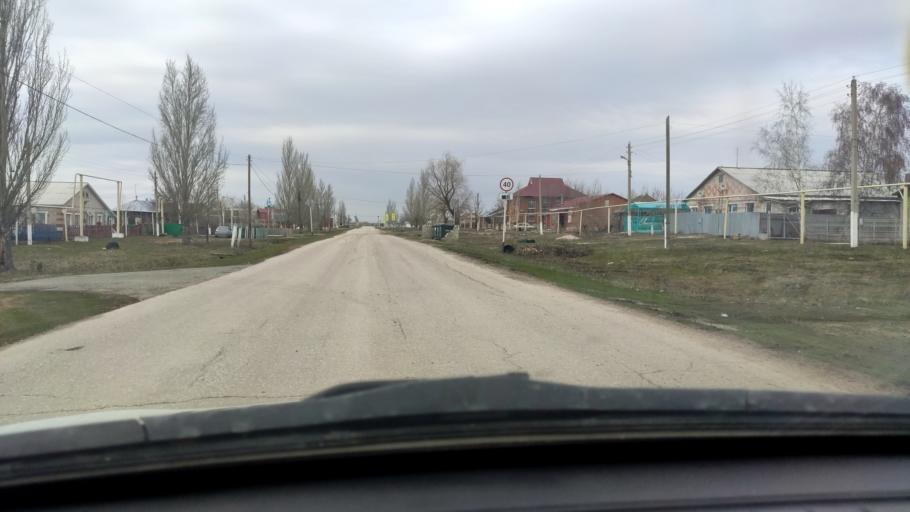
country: RU
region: Samara
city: Mezhdurechensk
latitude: 53.2591
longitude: 49.3007
